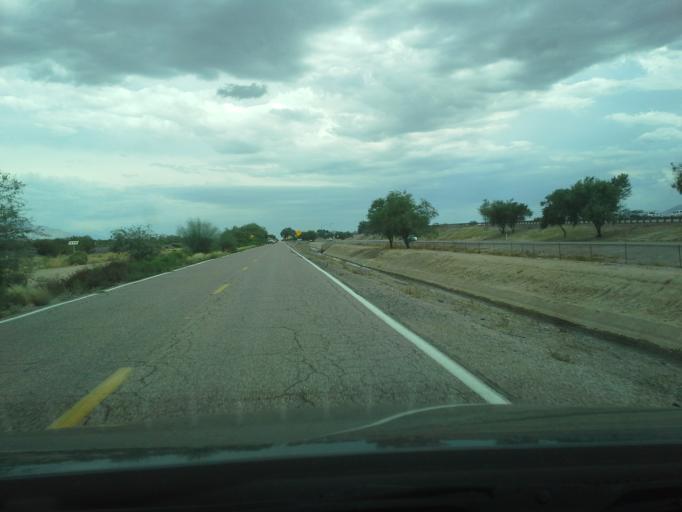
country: US
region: Arizona
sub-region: Pima County
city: Marana
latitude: 32.4650
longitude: -111.2195
